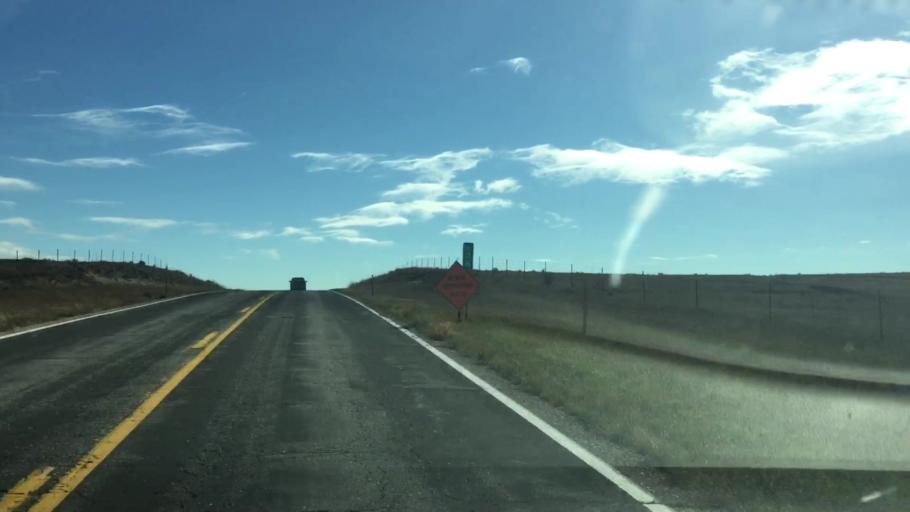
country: US
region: Colorado
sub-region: Elbert County
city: Kiowa
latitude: 39.2736
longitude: -104.2439
